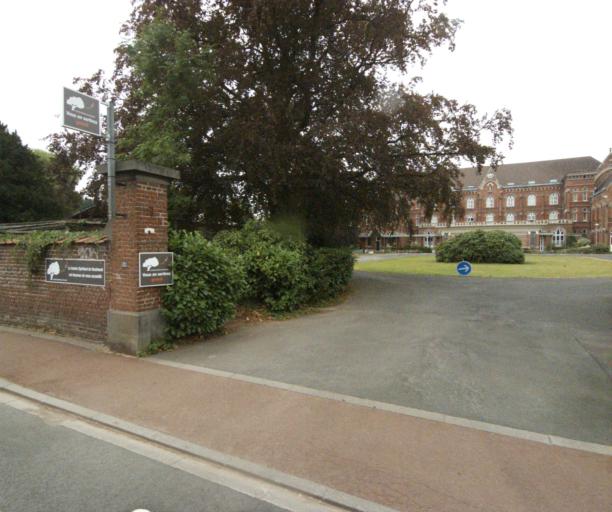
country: FR
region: Nord-Pas-de-Calais
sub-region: Departement du Nord
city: Mouvaux
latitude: 50.7057
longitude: 3.1303
